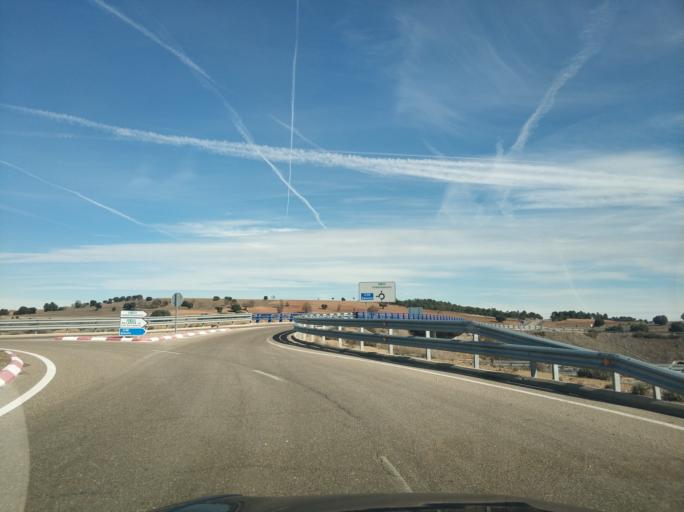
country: ES
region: Castille and Leon
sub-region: Provincia de Zamora
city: Cuelgamures
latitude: 41.2631
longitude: -5.7048
